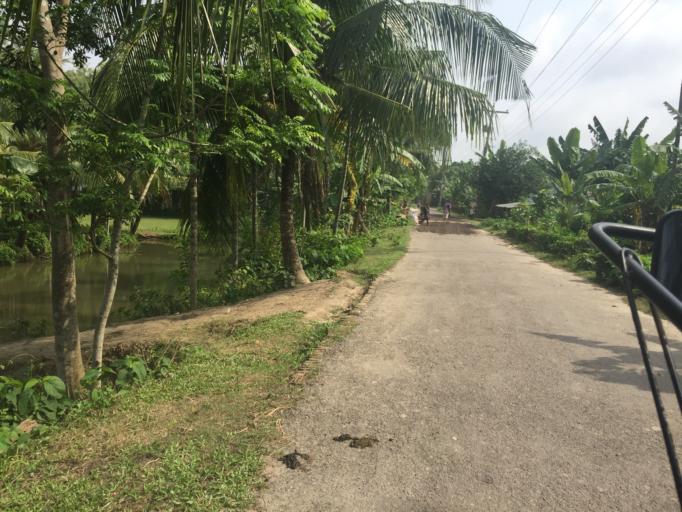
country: BD
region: Barisal
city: Mathba
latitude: 22.2296
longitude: 89.9157
